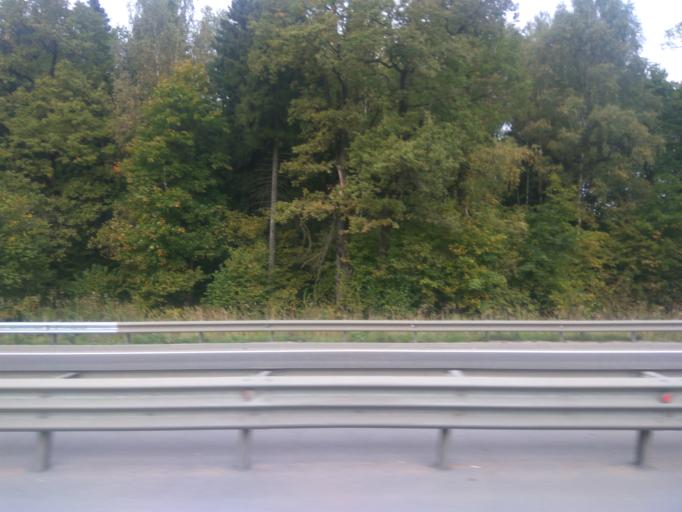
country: RU
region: Moskovskaya
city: Fryazino
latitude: 55.9448
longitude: 38.0404
